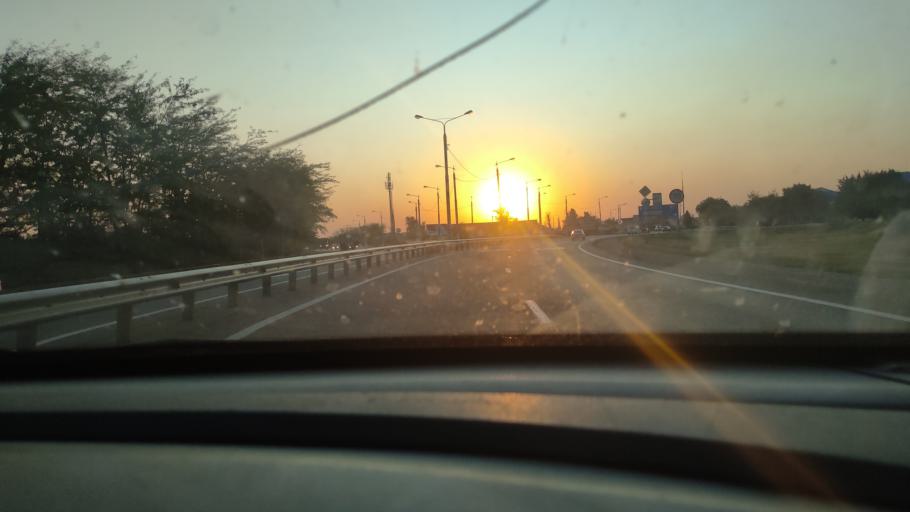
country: RU
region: Krasnodarskiy
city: Timashevsk
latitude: 45.6000
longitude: 38.9343
